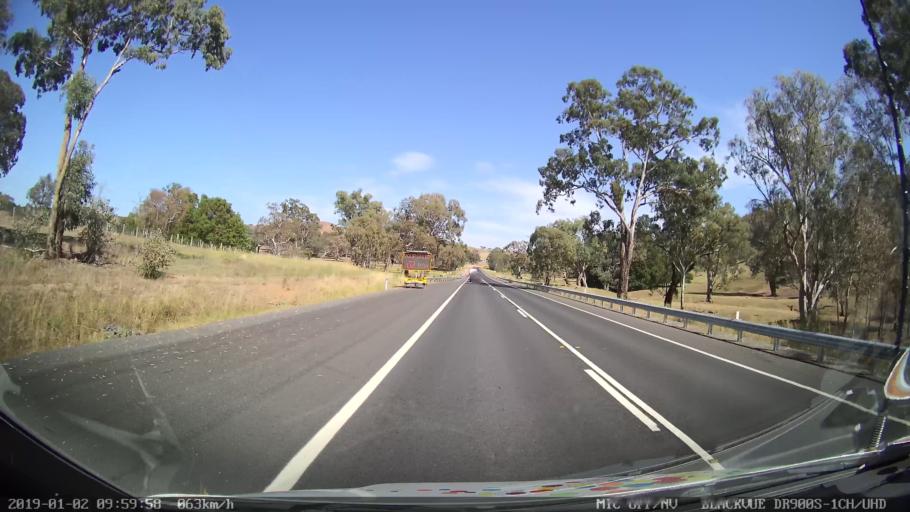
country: AU
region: New South Wales
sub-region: Gundagai
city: Gundagai
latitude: -35.1970
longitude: 148.1367
